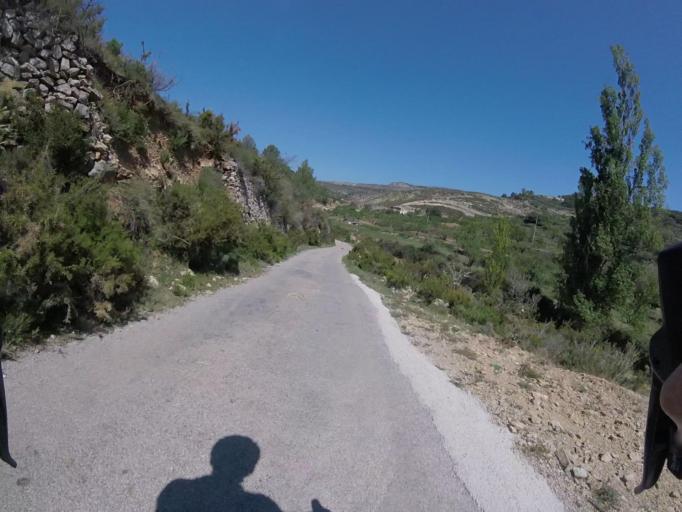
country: ES
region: Valencia
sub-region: Provincia de Castello
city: Sierra-Engarceran
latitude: 40.2601
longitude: -0.0229
